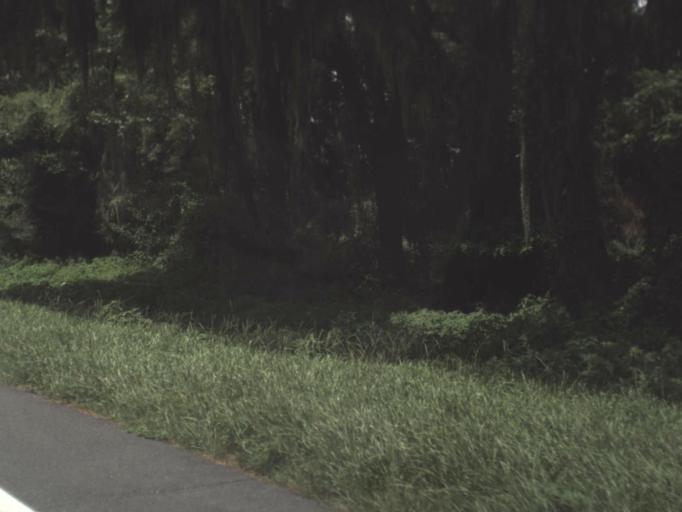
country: US
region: Florida
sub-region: Suwannee County
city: Wellborn
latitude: 30.3737
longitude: -82.8038
